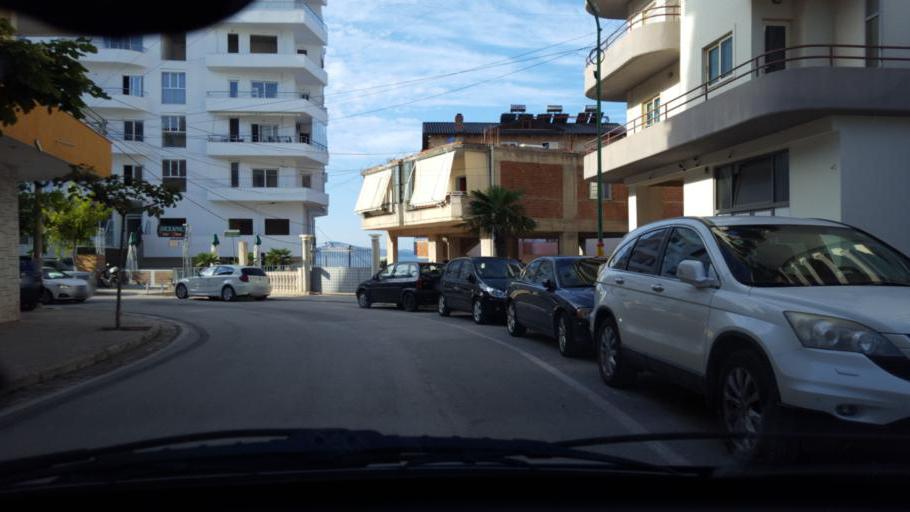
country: AL
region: Vlore
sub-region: Rrethi i Sarandes
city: Sarande
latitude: 39.8693
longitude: 19.9996
